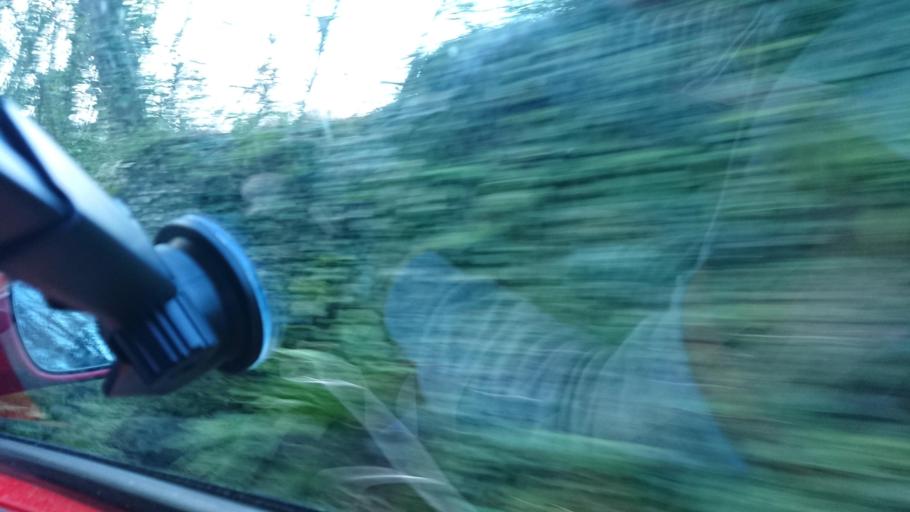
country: GB
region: England
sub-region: Cornwall
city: Looe
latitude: 50.3381
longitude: -4.4928
